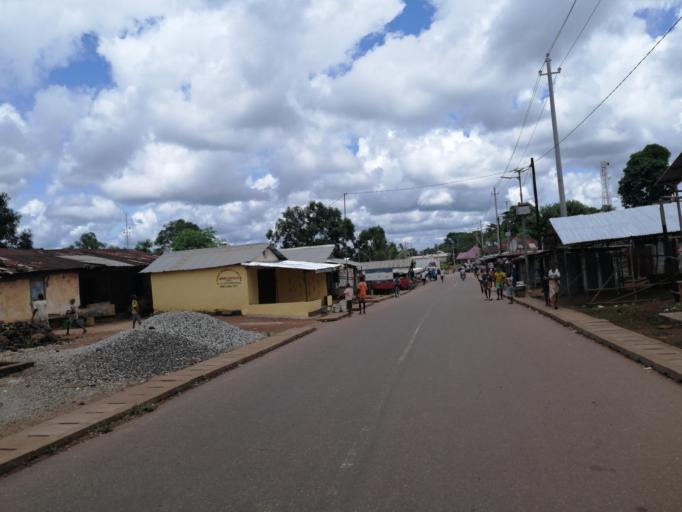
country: SL
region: Northern Province
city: Port Loko
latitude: 8.7726
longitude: -12.7886
